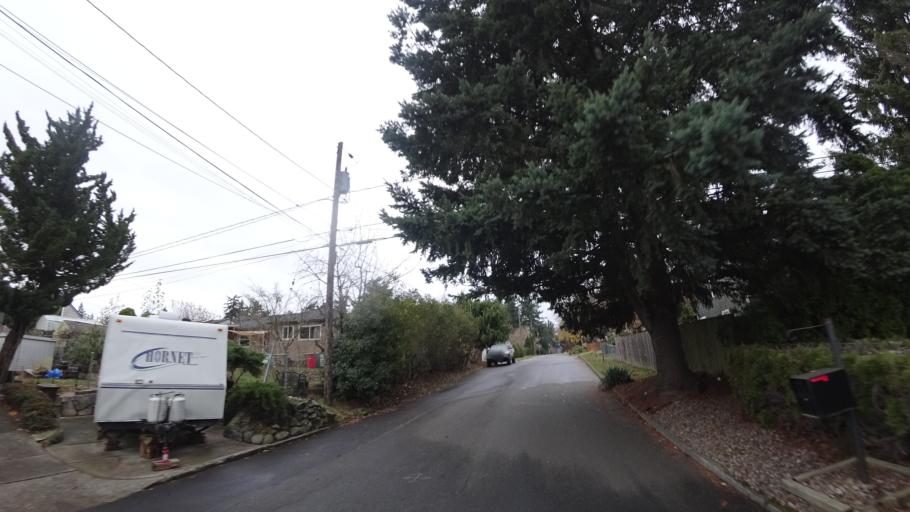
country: US
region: Oregon
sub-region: Multnomah County
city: Lents
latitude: 45.5147
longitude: -122.5465
